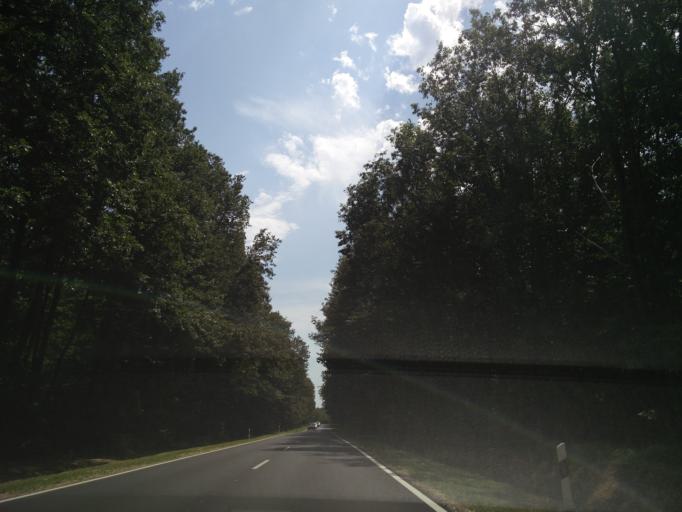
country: HU
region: Zala
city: Zalaegerszeg
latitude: 46.9055
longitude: 16.8584
